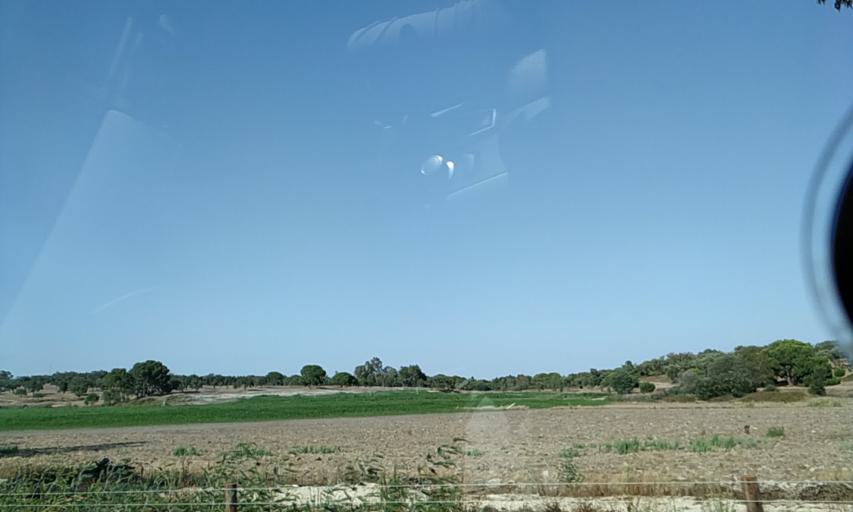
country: PT
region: Santarem
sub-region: Coruche
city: Coruche
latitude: 38.9939
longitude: -8.5549
